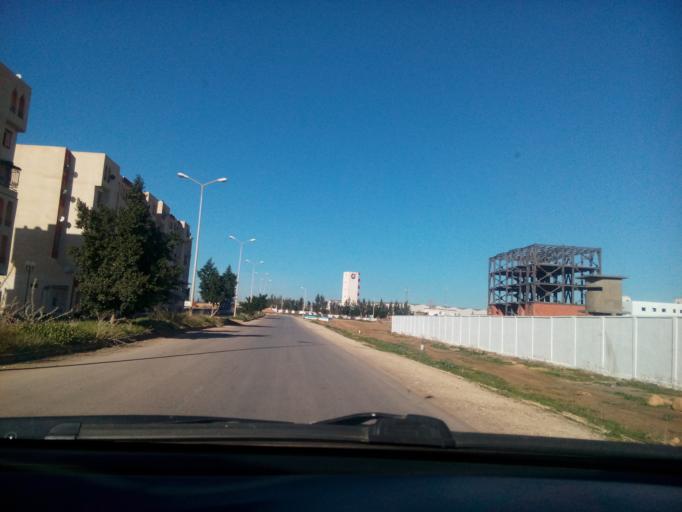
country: DZ
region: Relizane
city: Relizane
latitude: 35.7177
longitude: 0.5290
